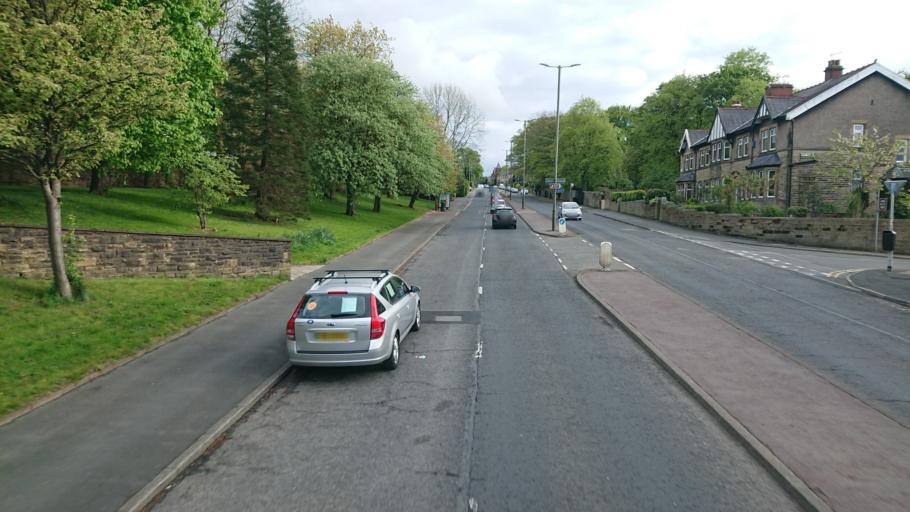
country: GB
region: England
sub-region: Lancashire
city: Burnley
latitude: 53.7827
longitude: -2.2535
